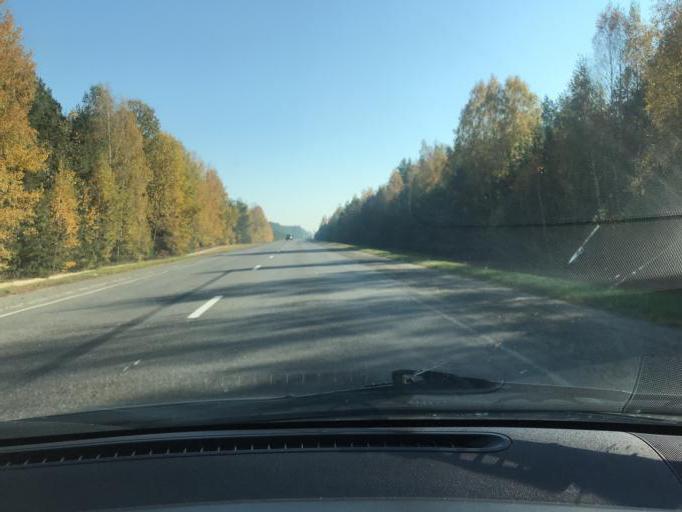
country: BY
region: Brest
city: Luninyets
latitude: 52.2689
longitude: 27.0014
